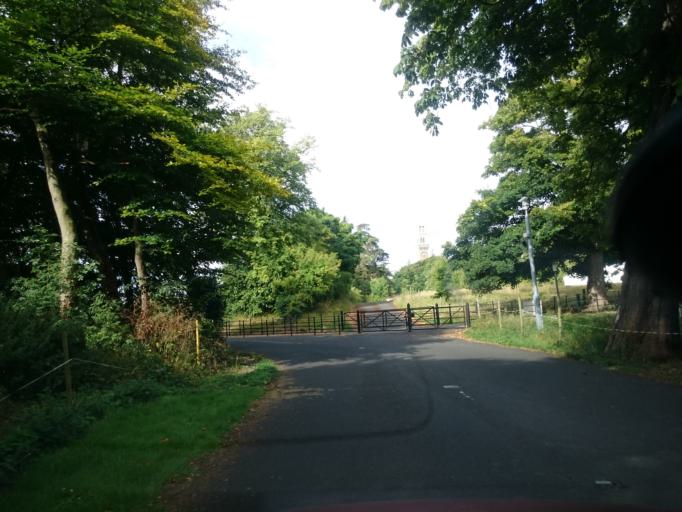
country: IE
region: Leinster
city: Castleknock
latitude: 53.3633
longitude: -6.3589
